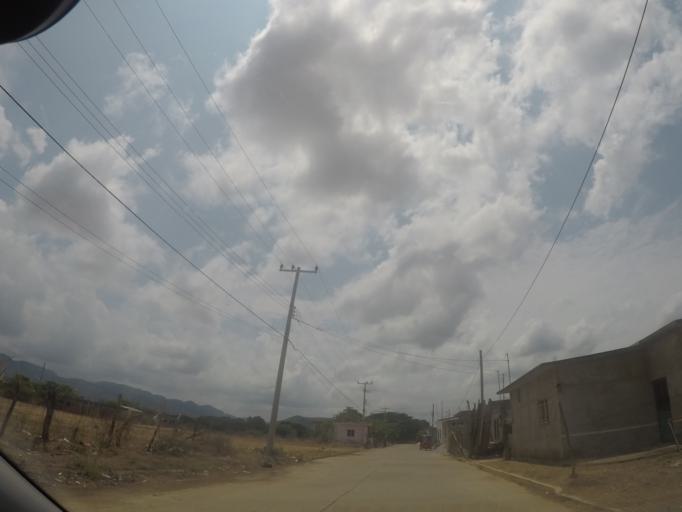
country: MX
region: Oaxaca
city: El Espinal
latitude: 16.5549
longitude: -94.9441
